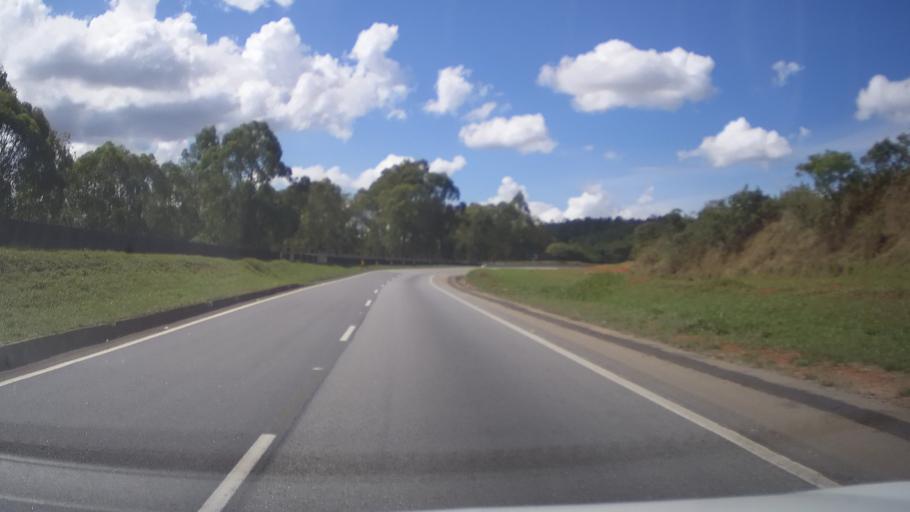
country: BR
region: Minas Gerais
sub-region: Santo Antonio Do Amparo
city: Santo Antonio do Amparo
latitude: -20.8645
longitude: -44.8409
